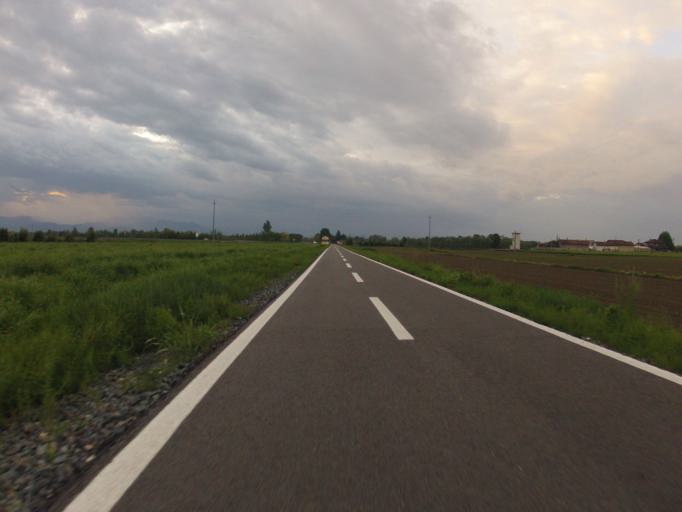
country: IT
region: Piedmont
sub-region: Provincia di Torino
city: Villafranca Piemonte
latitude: 44.8026
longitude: 7.5036
